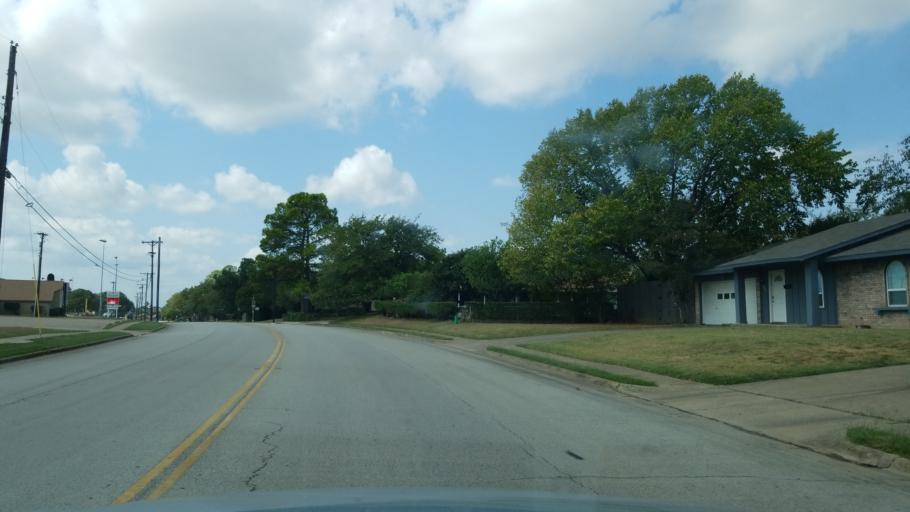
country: US
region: Texas
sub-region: Tarrant County
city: Euless
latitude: 32.8461
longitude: -97.0933
